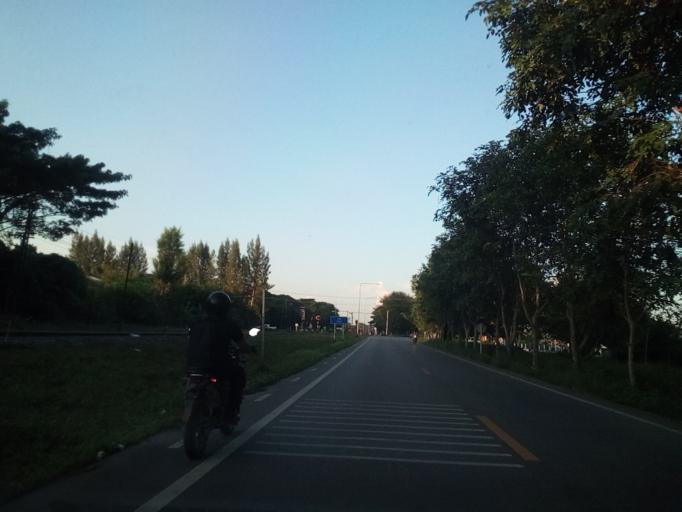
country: TH
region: Lamphun
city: Lamphun
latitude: 18.6349
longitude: 99.0416
